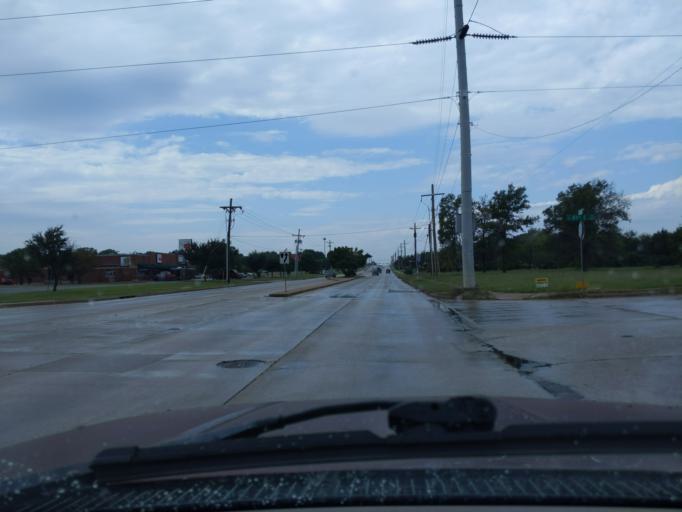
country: US
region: Oklahoma
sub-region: Tulsa County
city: Tulsa
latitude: 36.1336
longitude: -95.8776
